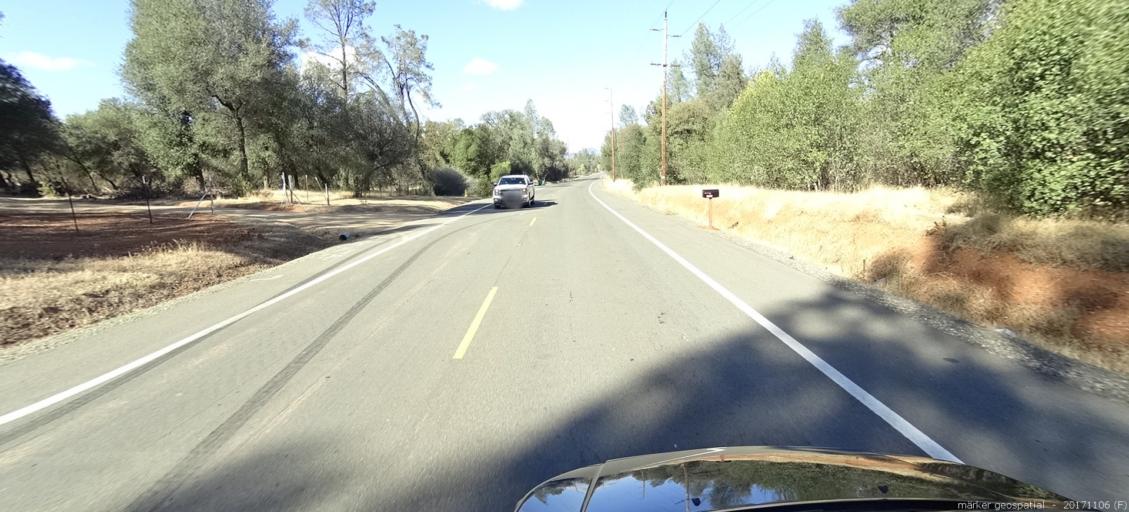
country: US
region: California
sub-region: Shasta County
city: Redding
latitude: 40.6007
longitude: -122.3133
